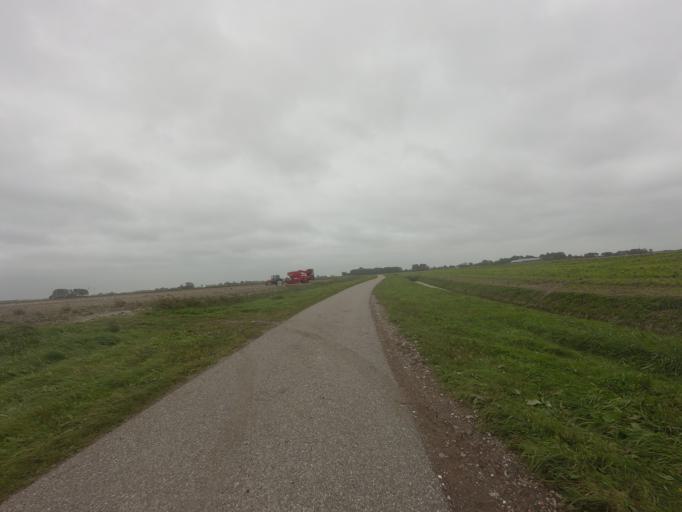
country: NL
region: Friesland
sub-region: Gemeente Ferwerderadiel
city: Ferwert
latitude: 53.3449
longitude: 5.8577
